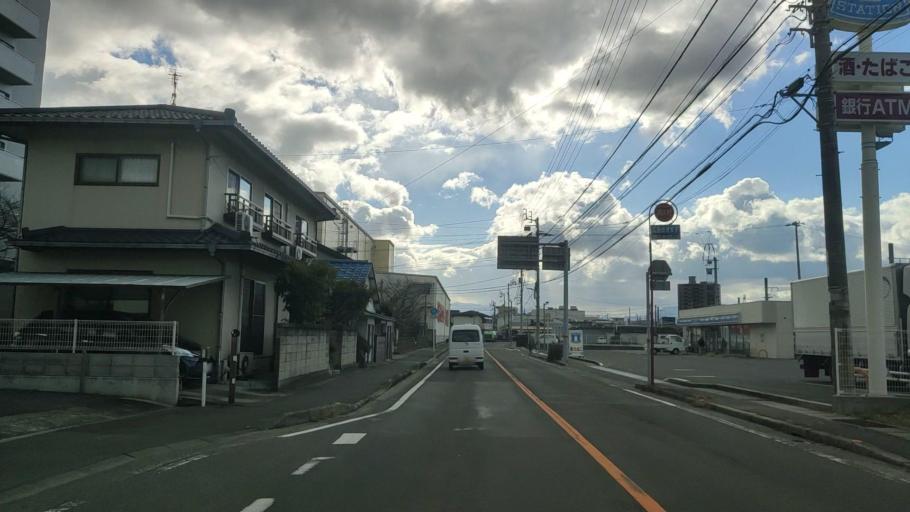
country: JP
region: Ehime
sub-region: Shikoku-chuo Shi
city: Matsuyama
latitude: 33.8670
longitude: 132.7186
